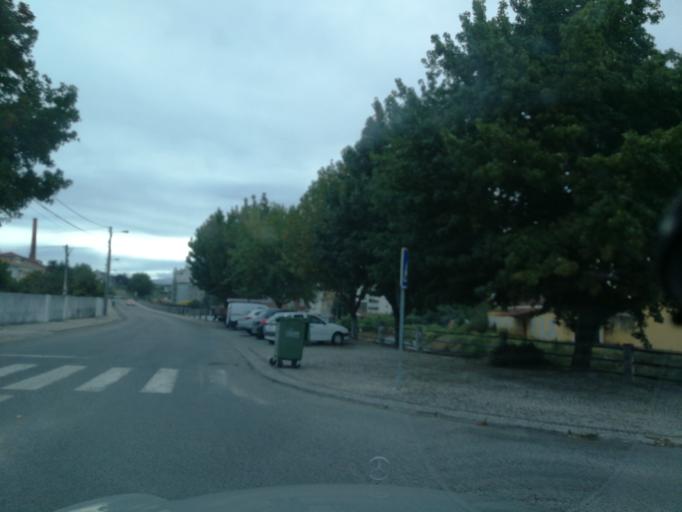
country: PT
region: Aveiro
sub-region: Agueda
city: Agueda
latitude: 40.5775
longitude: -8.4499
